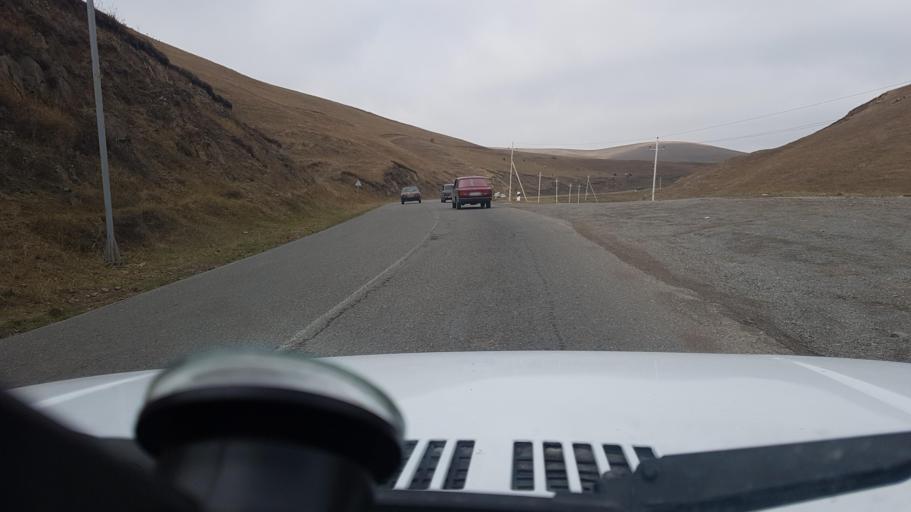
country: AZ
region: Gadabay Rayon
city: Ariqdam
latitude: 40.6140
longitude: 45.8120
